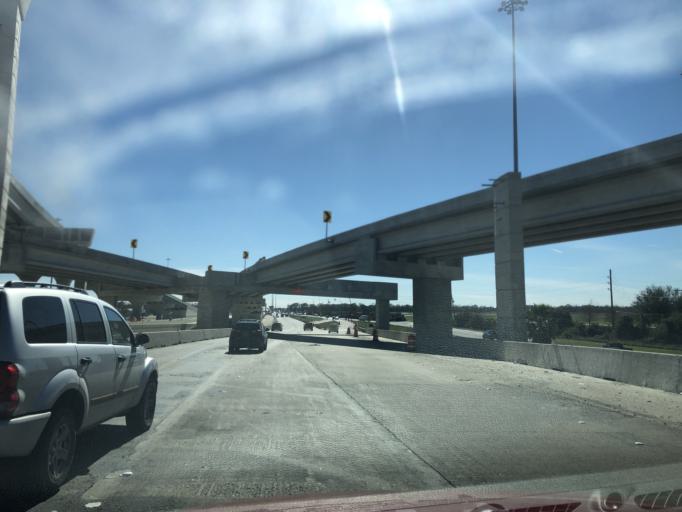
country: US
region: Texas
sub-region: Brazoria County
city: Brookside Village
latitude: 29.5953
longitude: -95.3868
